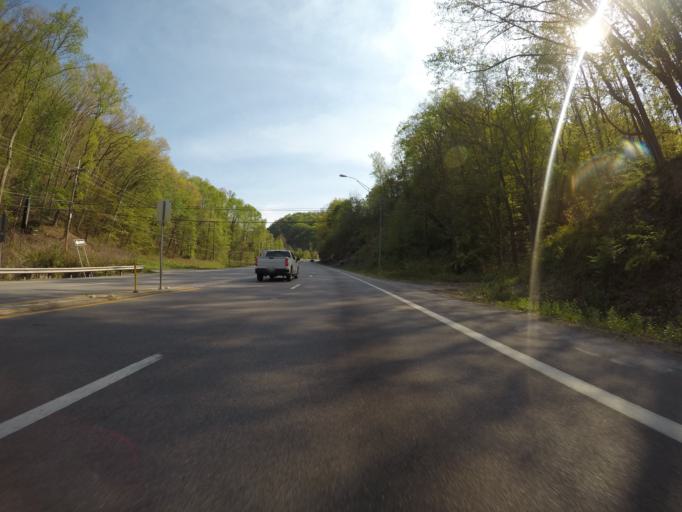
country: US
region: West Virginia
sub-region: Kanawha County
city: Charleston
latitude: 38.3550
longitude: -81.5974
